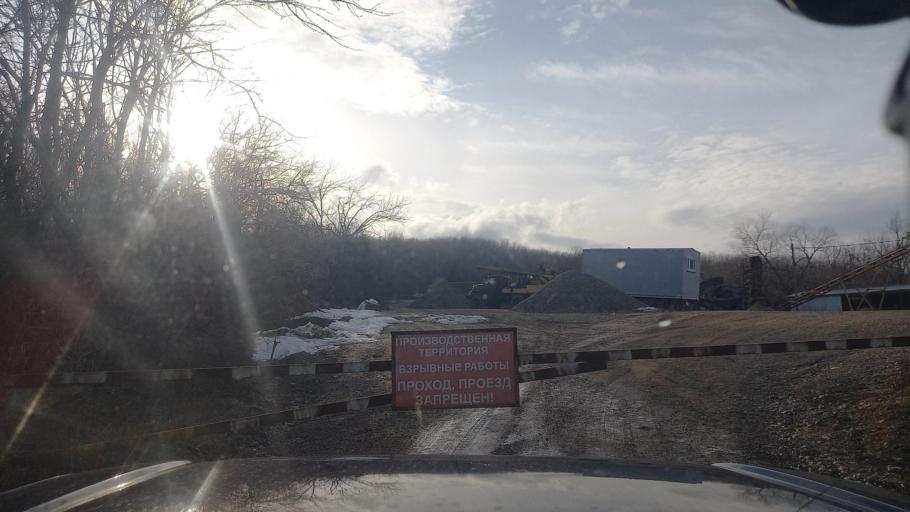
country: RU
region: Krasnodarskiy
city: Novodmitriyevskaya
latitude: 44.6967
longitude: 38.9623
